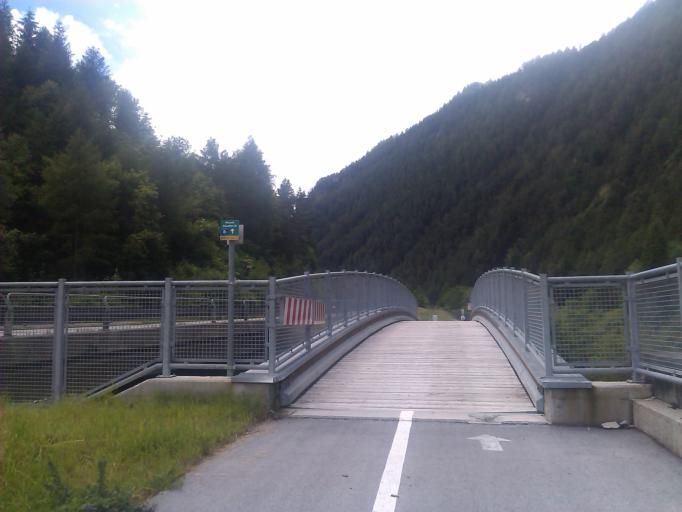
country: AT
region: Tyrol
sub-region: Politischer Bezirk Landeck
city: Ried im Oberinntal
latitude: 47.0421
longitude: 10.6344
